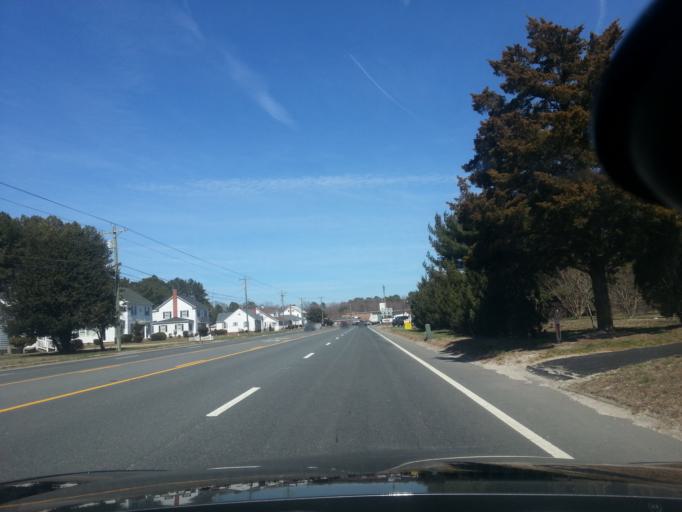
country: US
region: Virginia
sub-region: Accomack County
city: Accomac
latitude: 37.8172
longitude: -75.5892
